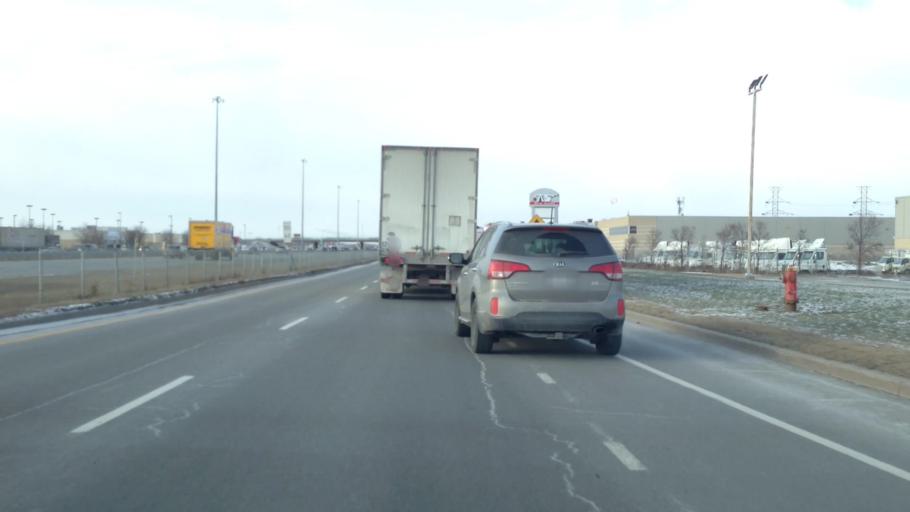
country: CA
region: Quebec
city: Dollard-Des Ormeaux
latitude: 45.5264
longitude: -73.7789
